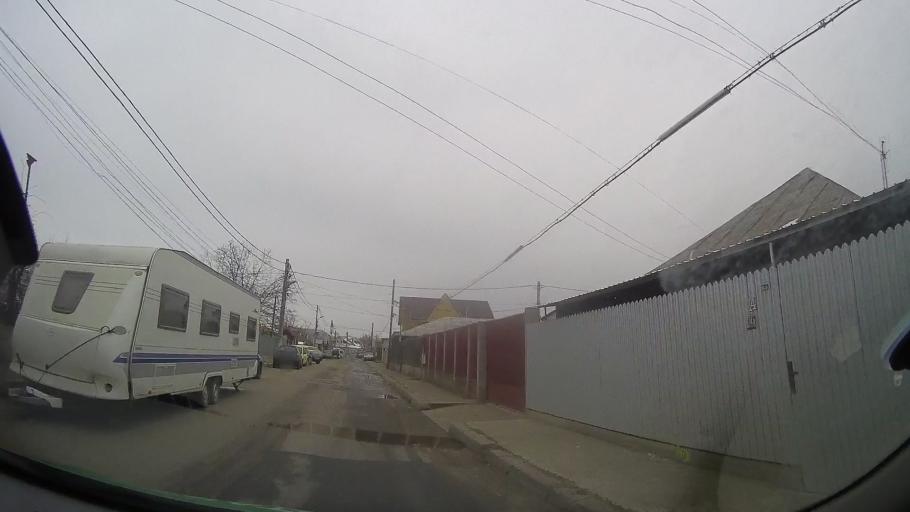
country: RO
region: Vaslui
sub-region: Municipiul Barlad
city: Barlad
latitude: 46.2355
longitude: 27.6788
